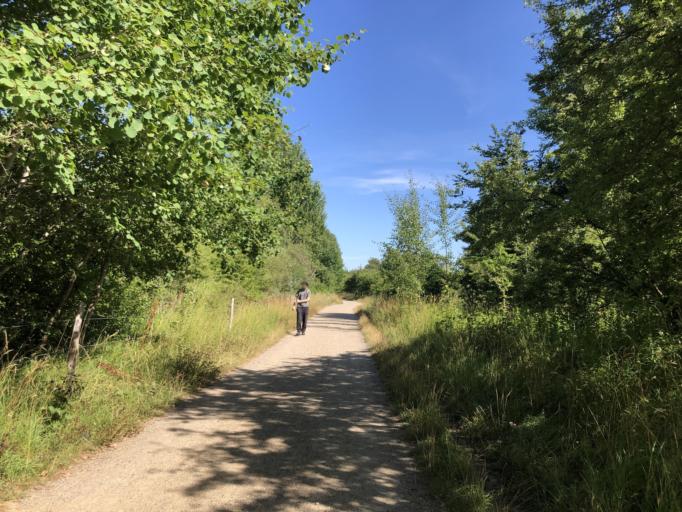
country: DK
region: Capital Region
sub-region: Kobenhavn
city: Copenhagen
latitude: 55.6558
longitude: 12.5765
